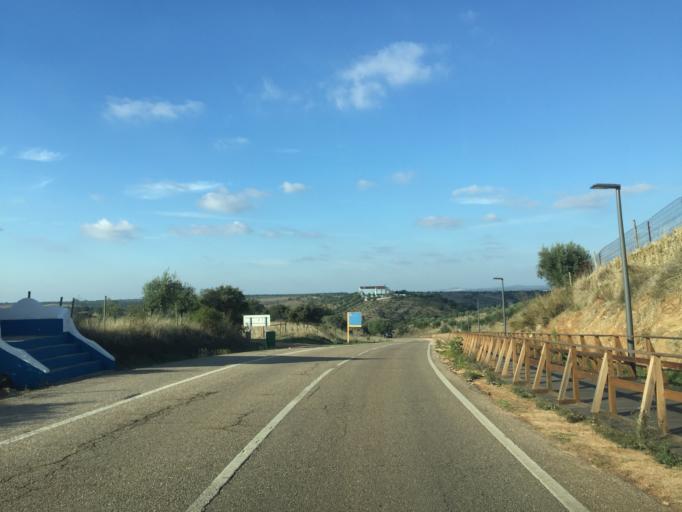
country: PT
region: Portalegre
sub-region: Fronteira
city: Fronteira
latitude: 39.0632
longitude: -7.6512
